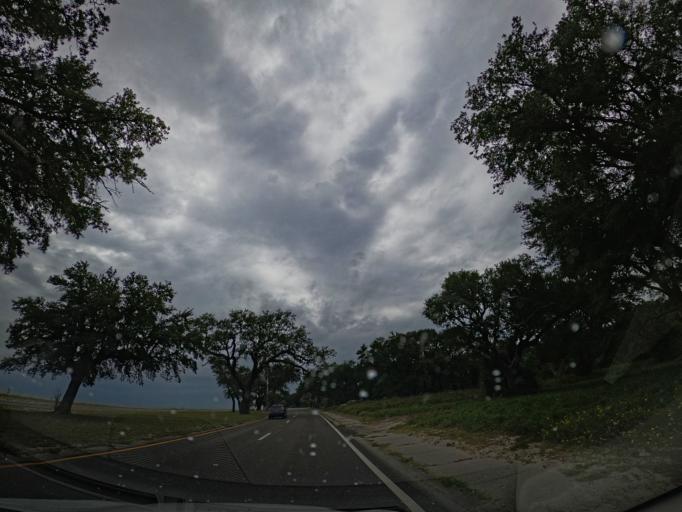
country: US
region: Mississippi
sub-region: Harrison County
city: Pass Christian
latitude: 30.3110
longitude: -89.2582
